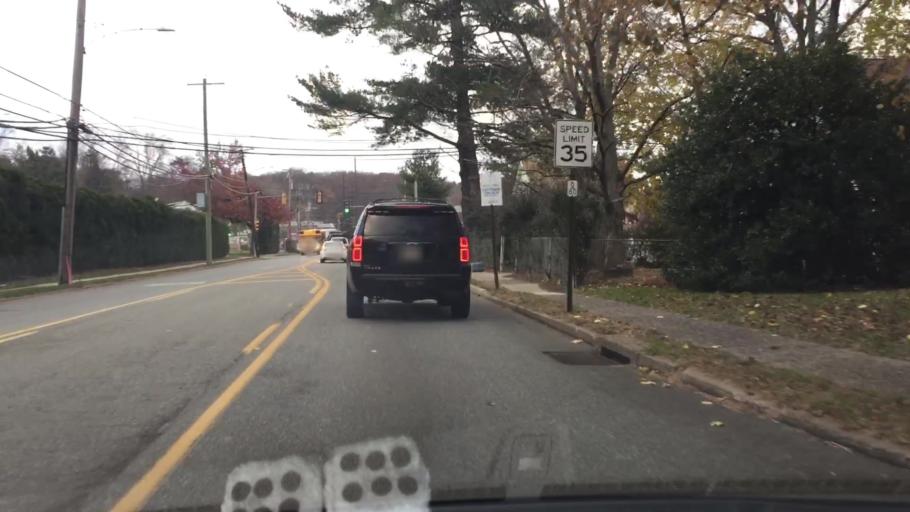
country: US
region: Pennsylvania
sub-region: Delaware County
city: Morton
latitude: 39.9121
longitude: -75.3089
